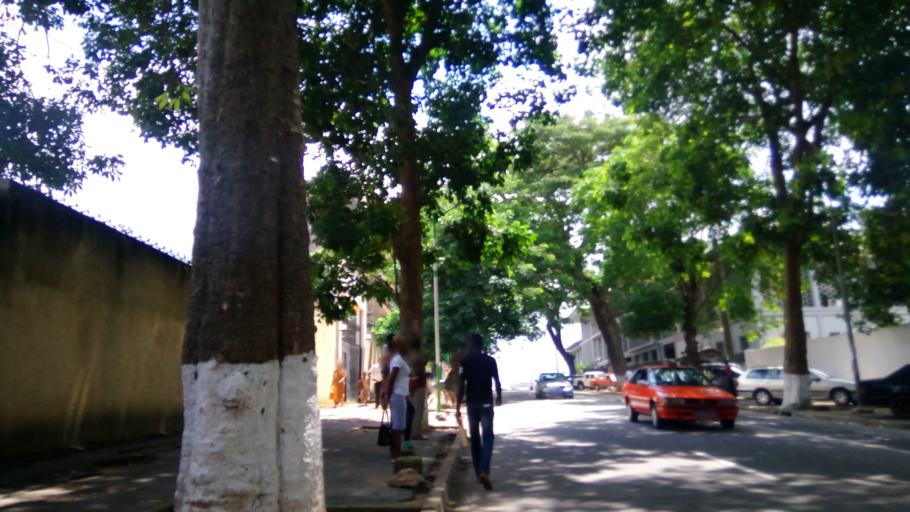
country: CI
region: Lagunes
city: Abidjan
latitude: 5.3301
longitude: -4.0207
